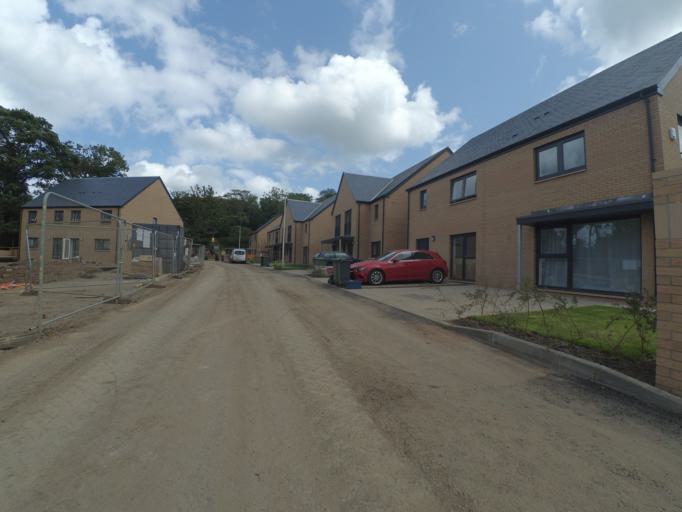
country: GB
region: Scotland
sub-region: Midlothian
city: Bonnyrigg
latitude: 55.9152
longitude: -3.1254
